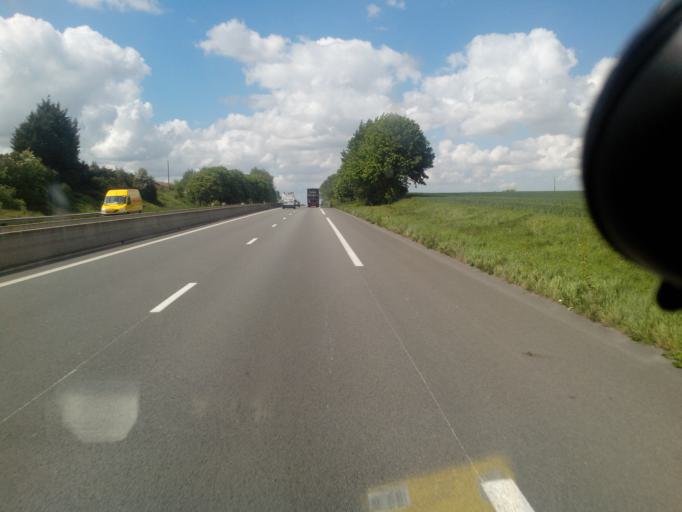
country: FR
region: Nord-Pas-de-Calais
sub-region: Departement du Nord
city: Godewaersvelde
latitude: 50.7657
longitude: 2.6389
